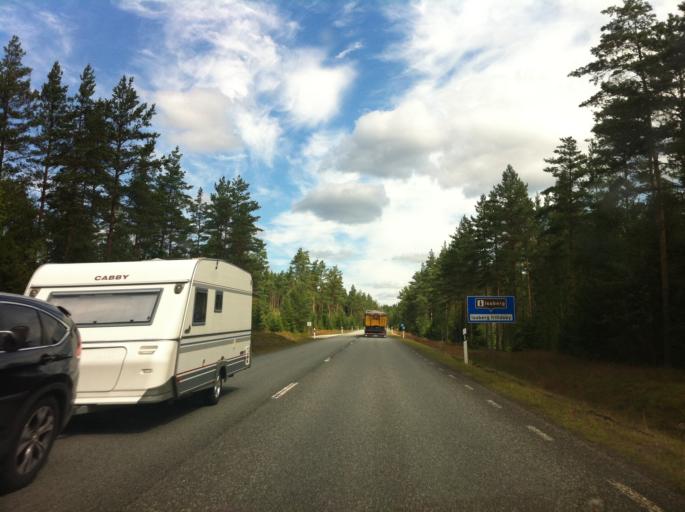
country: SE
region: Joenkoeping
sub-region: Gislaveds Kommun
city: Gislaved
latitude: 57.4133
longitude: 13.6005
